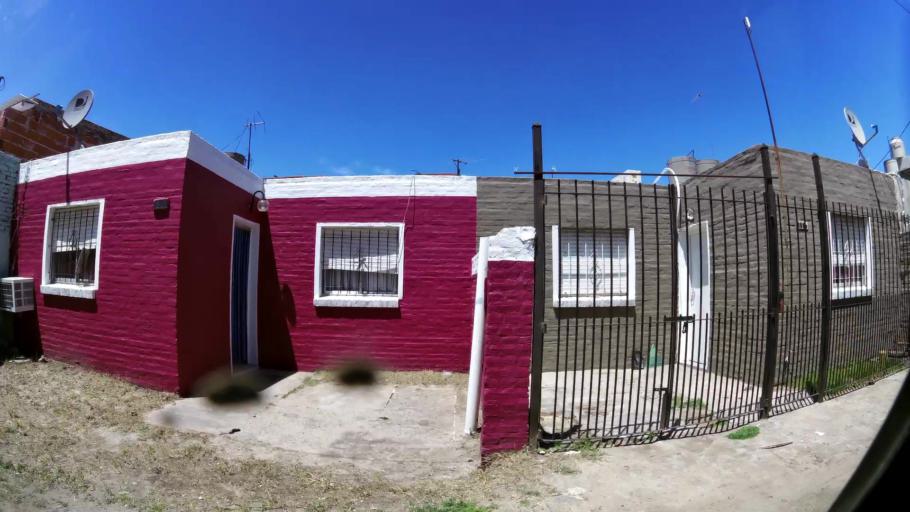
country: AR
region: Buenos Aires
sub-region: Partido de Quilmes
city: Quilmes
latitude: -34.7196
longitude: -58.3210
